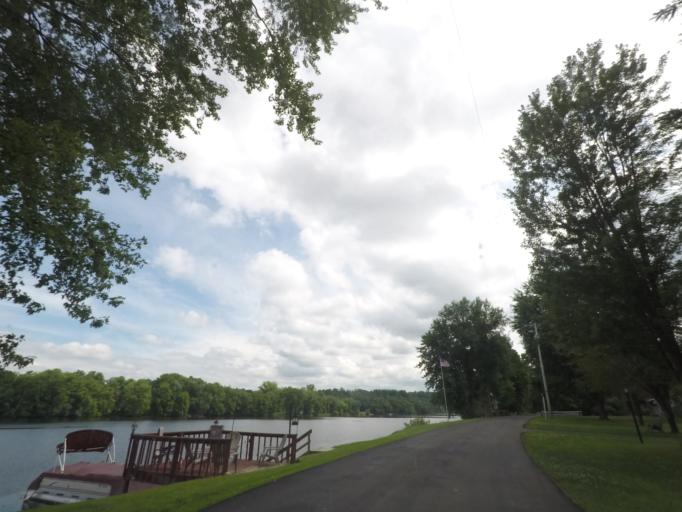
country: US
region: New York
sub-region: Saratoga County
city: Stillwater
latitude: 42.9895
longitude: -73.6096
